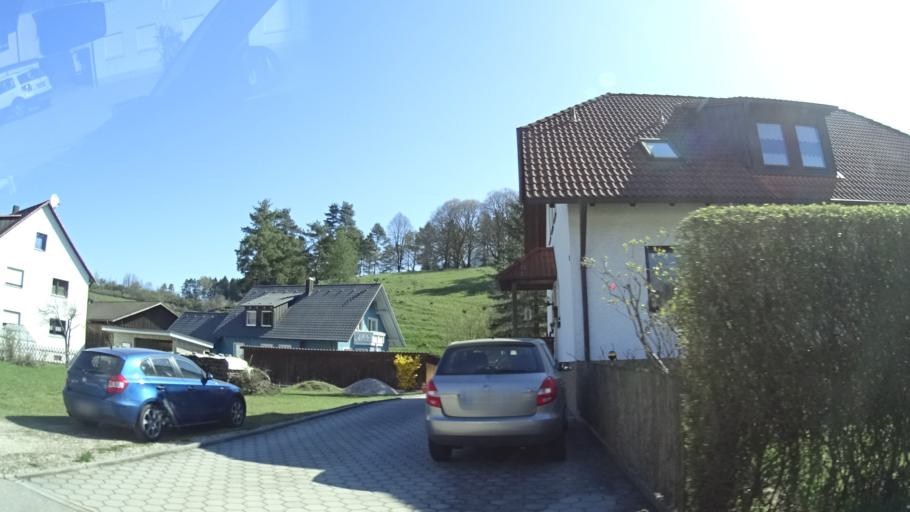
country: DE
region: Bavaria
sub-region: Regierungsbezirk Mittelfranken
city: Alfeld
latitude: 49.4250
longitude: 11.5442
